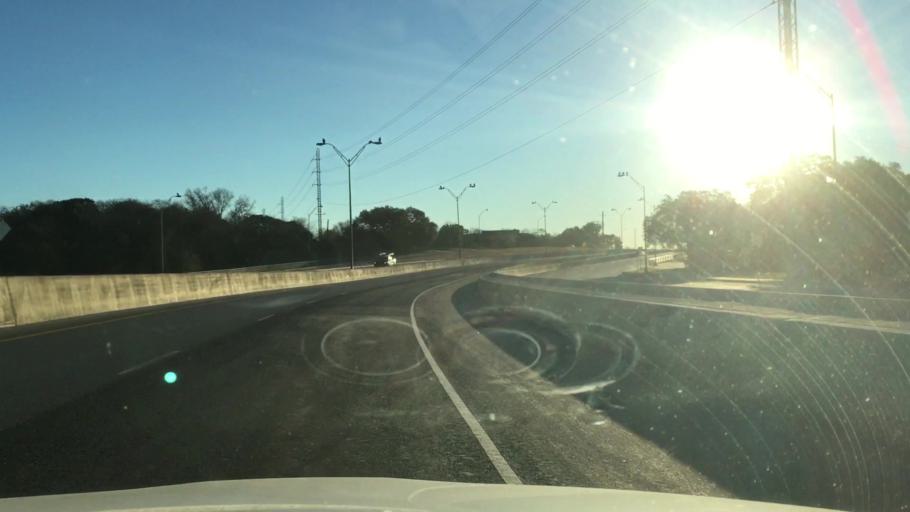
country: US
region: Texas
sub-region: Bexar County
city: Castle Hills
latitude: 29.5577
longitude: -98.4923
